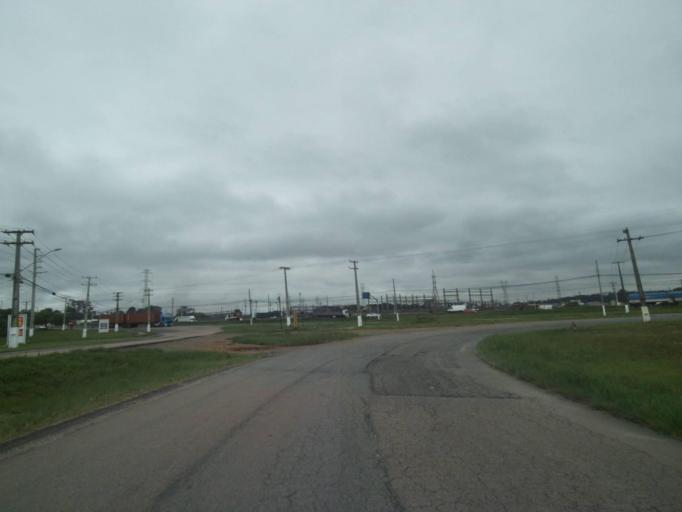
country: BR
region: Parana
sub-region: Araucaria
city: Araucaria
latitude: -25.5233
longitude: -49.3309
